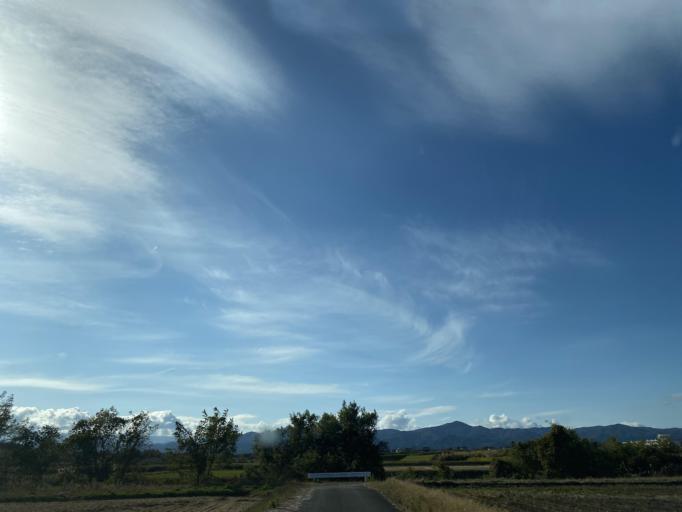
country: JP
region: Fukushima
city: Koriyama
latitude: 37.3601
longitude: 140.3313
